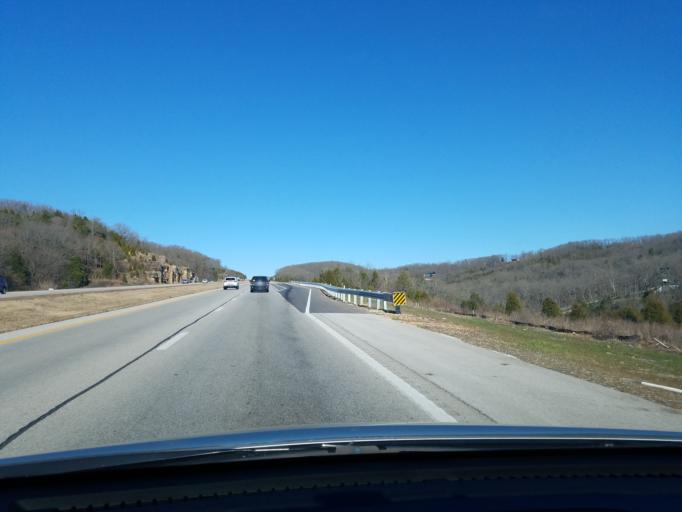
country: US
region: Missouri
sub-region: Taney County
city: Merriam Woods
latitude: 36.7791
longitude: -93.2244
